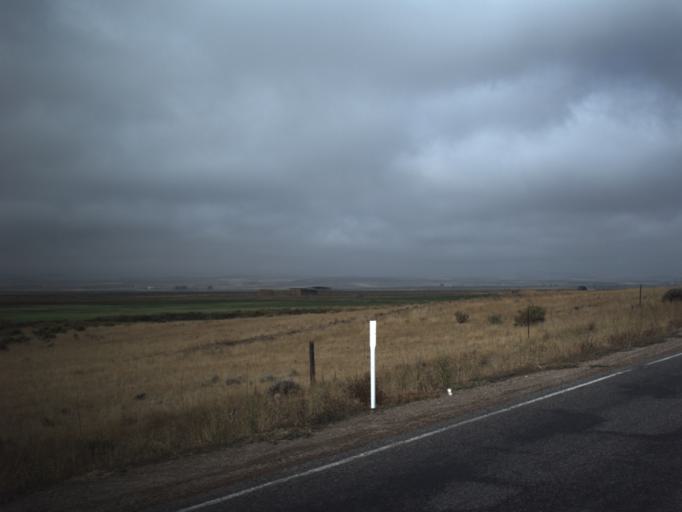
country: US
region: Utah
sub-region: Rich County
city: Randolph
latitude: 41.4775
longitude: -111.1130
